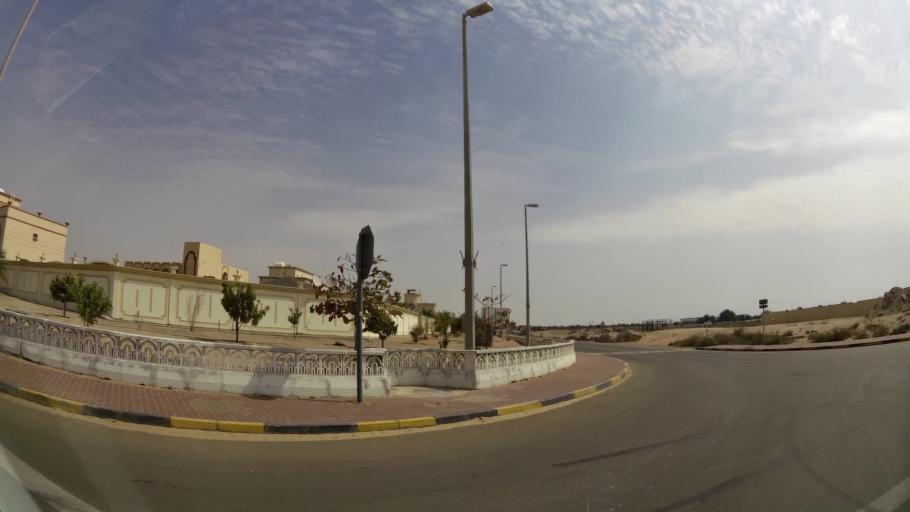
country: AE
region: Abu Dhabi
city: Abu Dhabi
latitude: 24.5451
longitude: 54.6607
